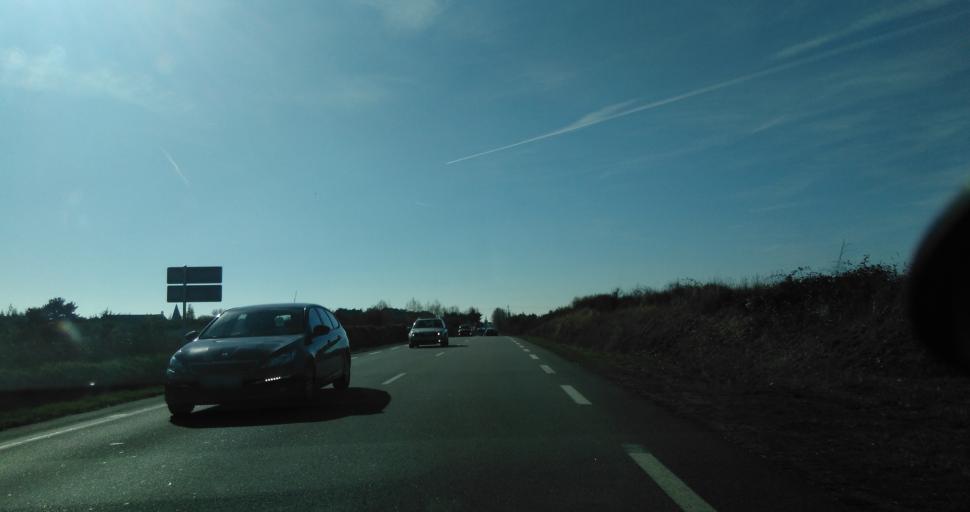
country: FR
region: Brittany
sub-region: Departement du Morbihan
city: Plouharnel
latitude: 47.6083
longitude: -3.0970
